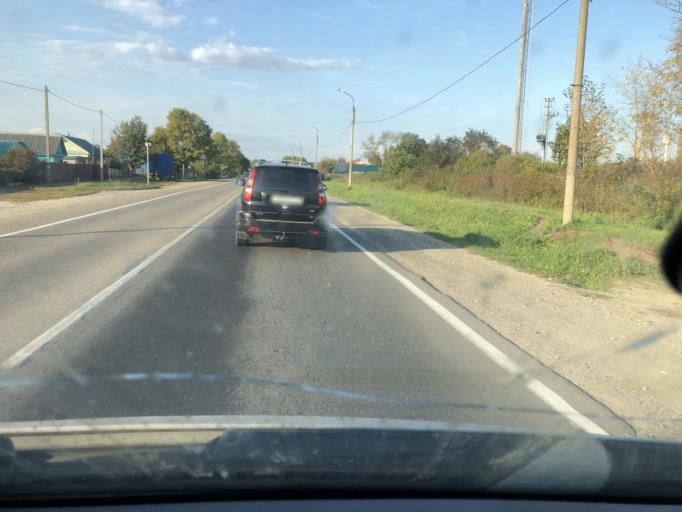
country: RU
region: Kaluga
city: Peremyshl'
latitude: 54.3778
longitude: 36.1976
